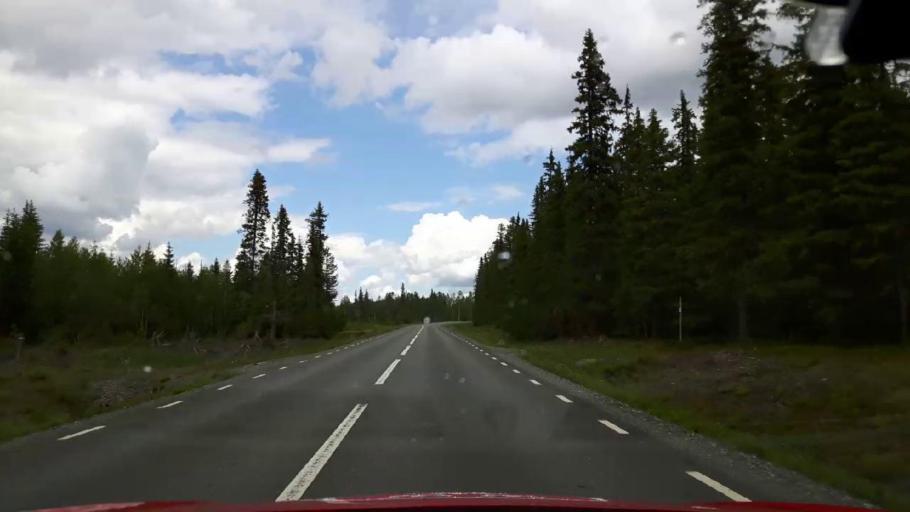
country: SE
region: Jaemtland
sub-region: Krokoms Kommun
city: Krokom
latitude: 63.5775
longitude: 14.2827
